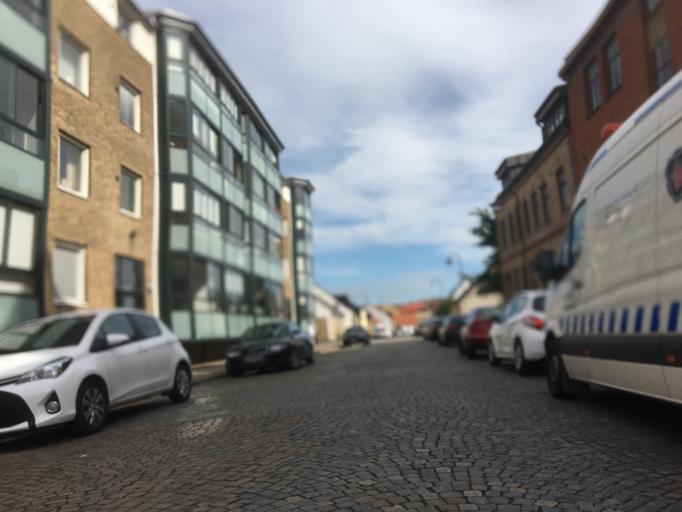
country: SE
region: Skane
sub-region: Landskrona
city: Landskrona
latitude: 55.8783
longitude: 12.8344
